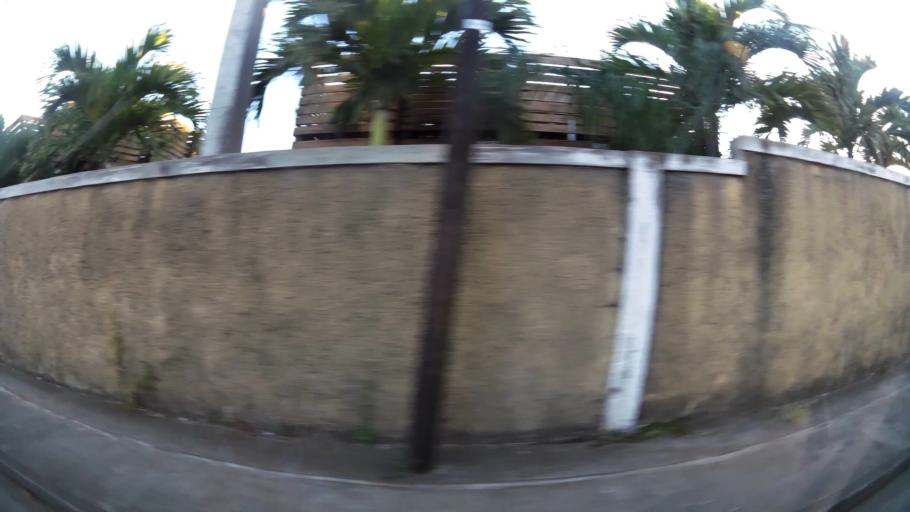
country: MU
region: Moka
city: Moka
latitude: -20.2224
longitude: 57.5030
